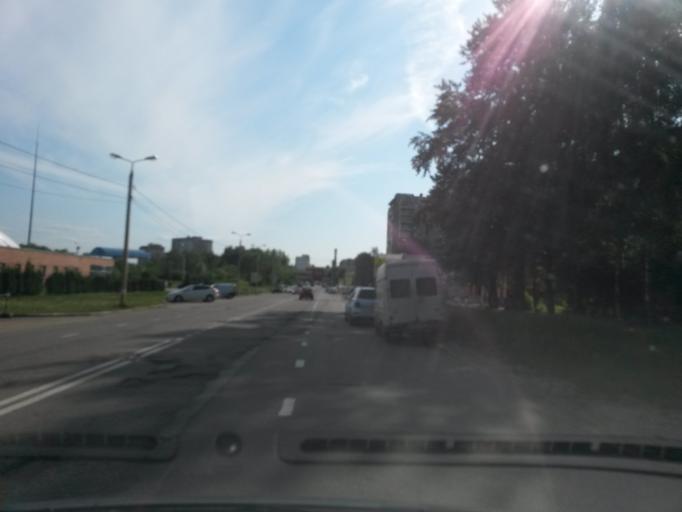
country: RU
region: Jaroslavl
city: Yaroslavl
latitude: 57.6889
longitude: 39.7715
